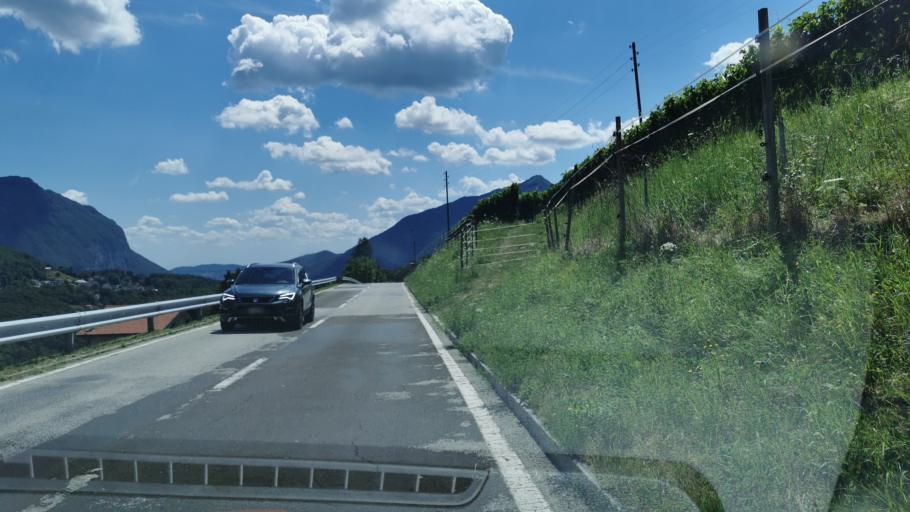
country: IT
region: Lombardy
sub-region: Provincia di Como
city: Campione
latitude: 45.9531
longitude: 8.9832
